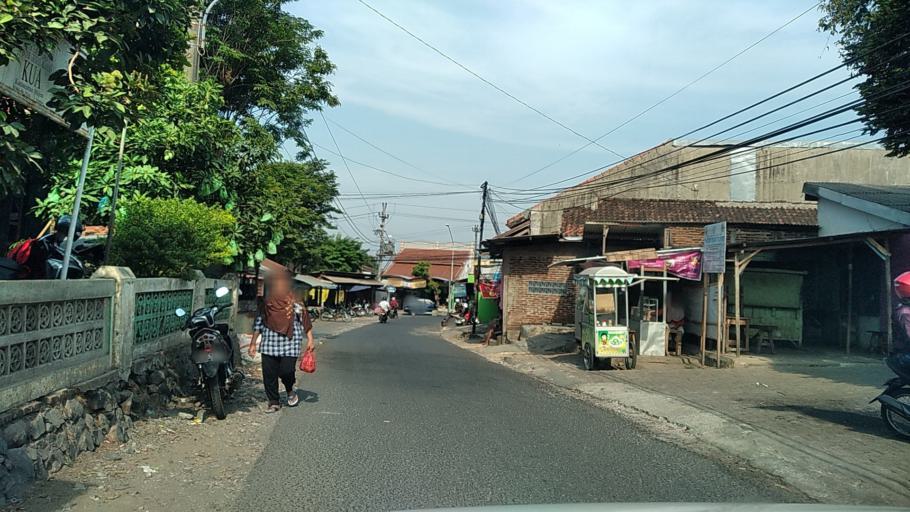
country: ID
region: Central Java
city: Semarang
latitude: -7.0519
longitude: 110.3164
